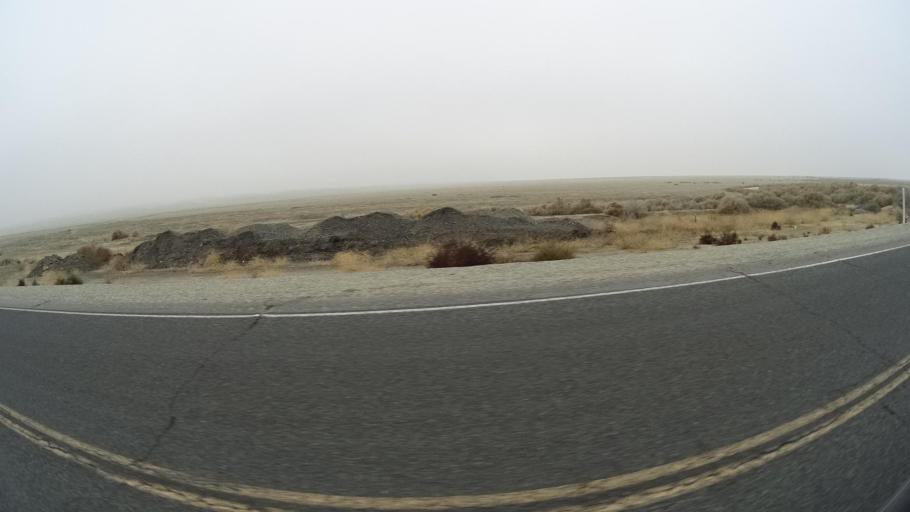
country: US
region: California
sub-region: Kern County
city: Buttonwillow
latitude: 35.3451
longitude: -119.4688
